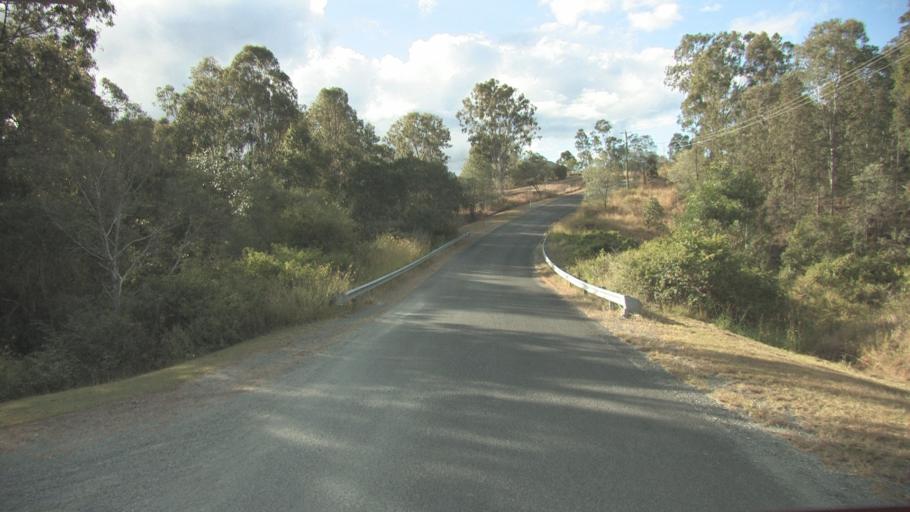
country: AU
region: Queensland
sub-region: Logan
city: Cedar Vale
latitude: -27.9054
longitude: 153.0640
